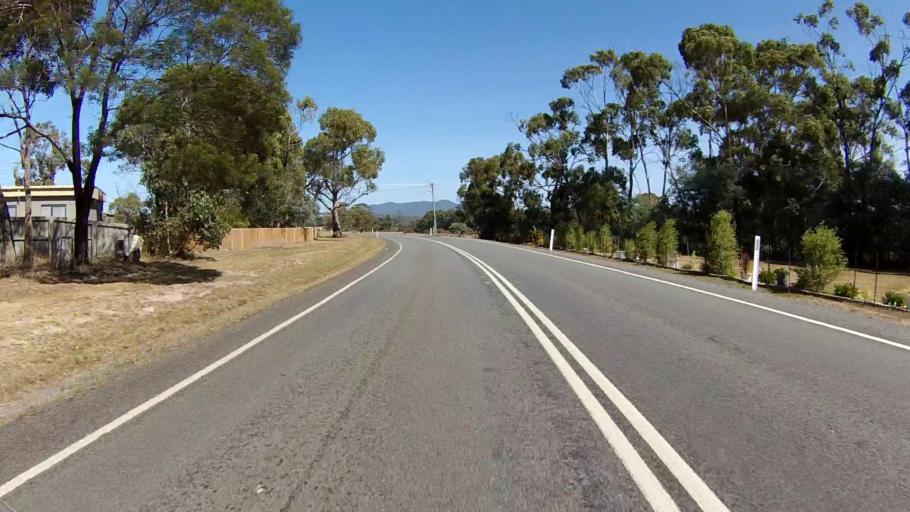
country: AU
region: Tasmania
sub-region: Sorell
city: Sorell
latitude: -42.5039
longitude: 147.9085
